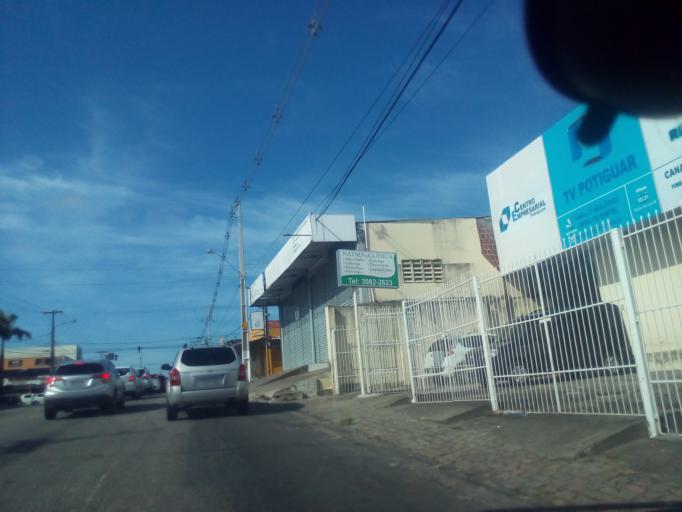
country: BR
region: Rio Grande do Norte
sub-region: Natal
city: Natal
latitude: -5.8111
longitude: -35.2120
